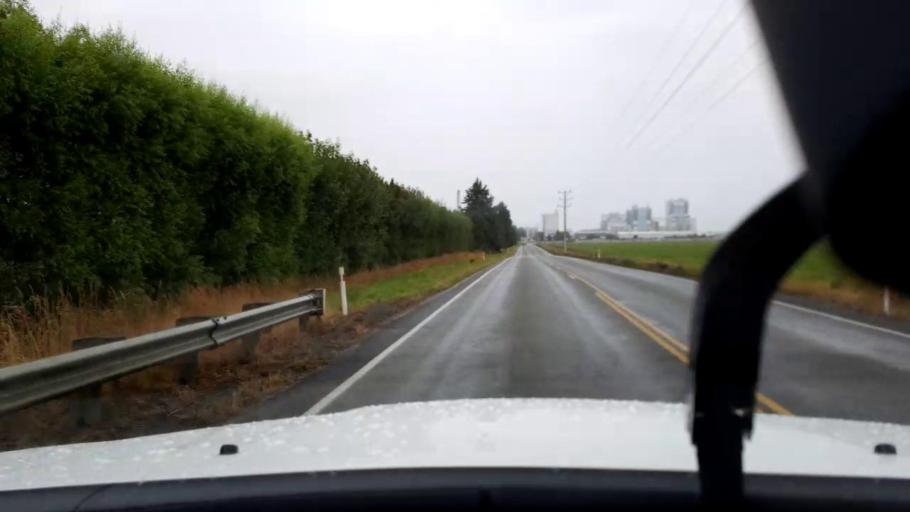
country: NZ
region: Canterbury
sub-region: Timaru District
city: Timaru
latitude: -44.2045
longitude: 171.3741
